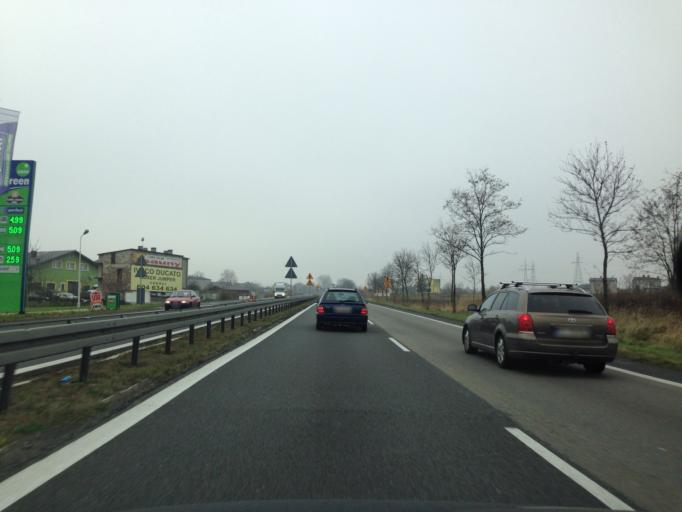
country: PL
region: Silesian Voivodeship
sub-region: Powiat bedzinski
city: Sarnow
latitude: 50.3783
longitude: 19.1585
